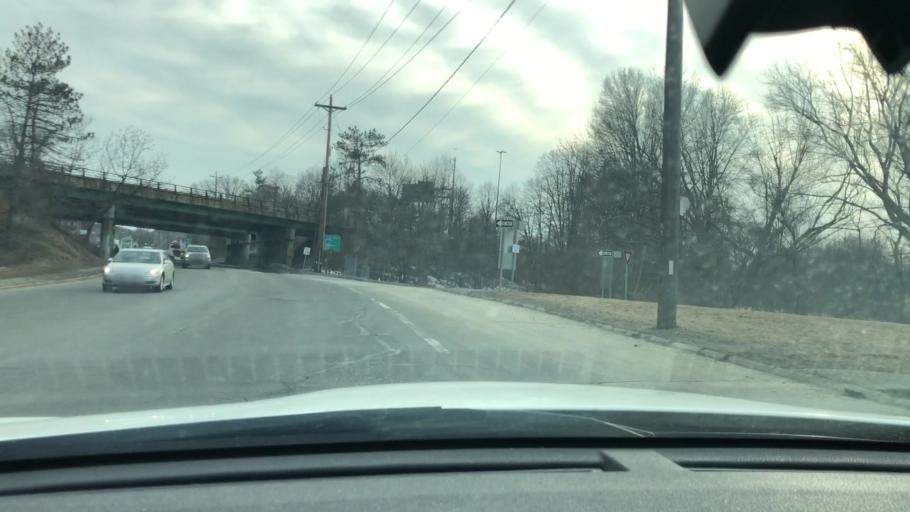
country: US
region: Massachusetts
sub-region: Middlesex County
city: Chelmsford
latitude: 42.6061
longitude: -71.3440
